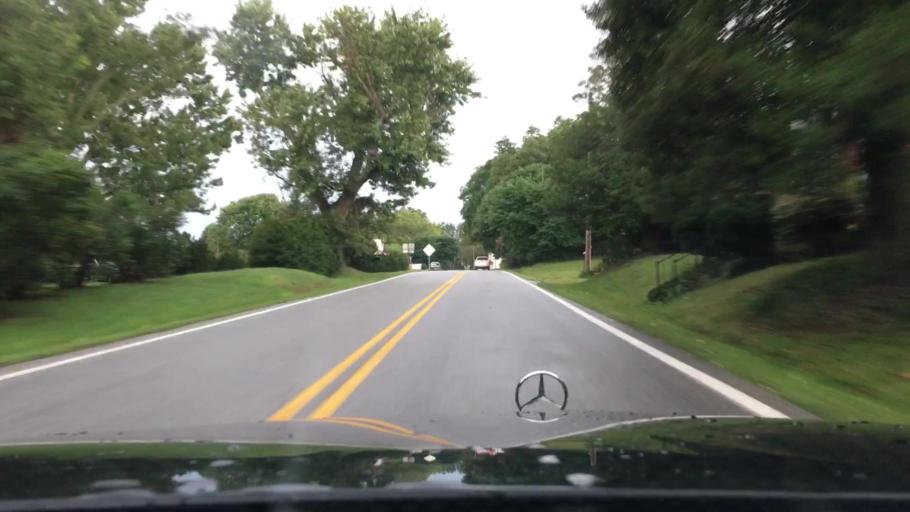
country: US
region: Virginia
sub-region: Amherst County
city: Amherst
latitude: 37.6433
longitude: -79.0223
